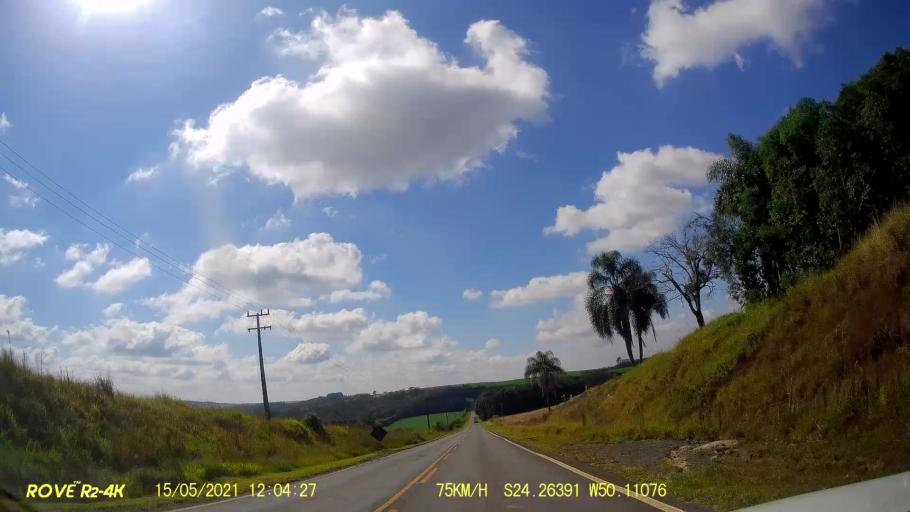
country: BR
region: Parana
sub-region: Pirai Do Sul
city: Pirai do Sul
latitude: -24.2640
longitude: -50.1108
